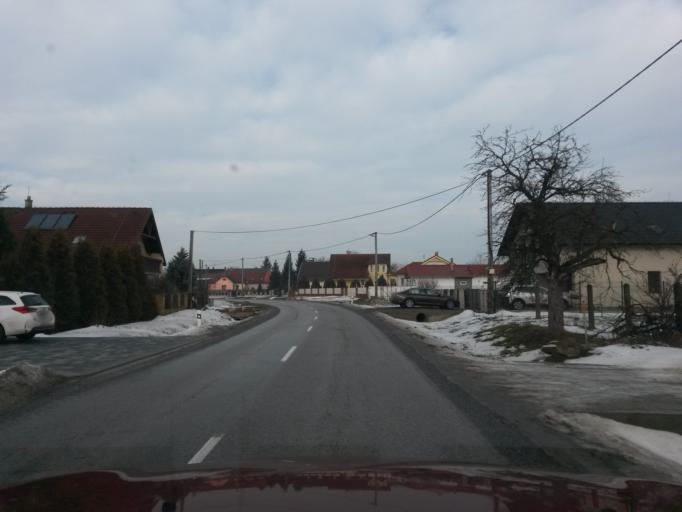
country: SK
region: Kosicky
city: Kosice
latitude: 48.7803
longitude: 21.3294
